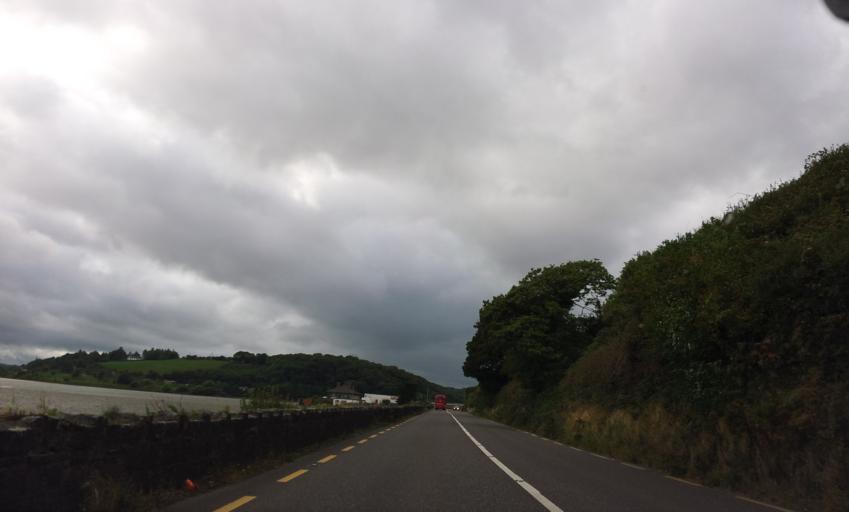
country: IE
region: Munster
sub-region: County Cork
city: Youghal
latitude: 51.9779
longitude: -7.8452
